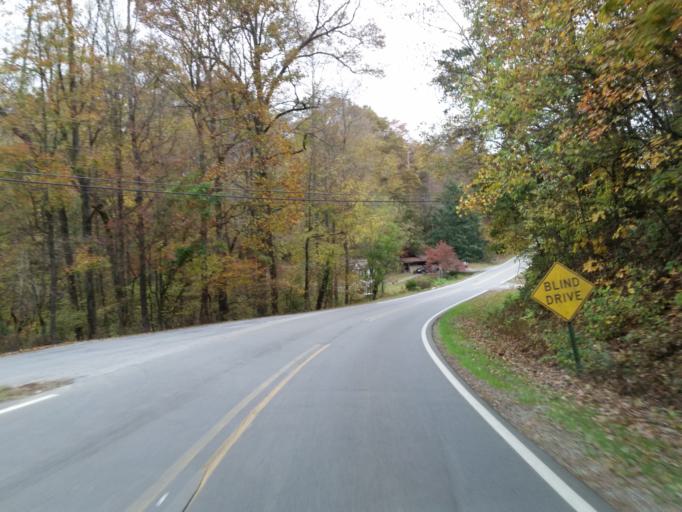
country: US
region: Georgia
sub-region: Gilmer County
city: Ellijay
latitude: 34.6607
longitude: -84.3795
